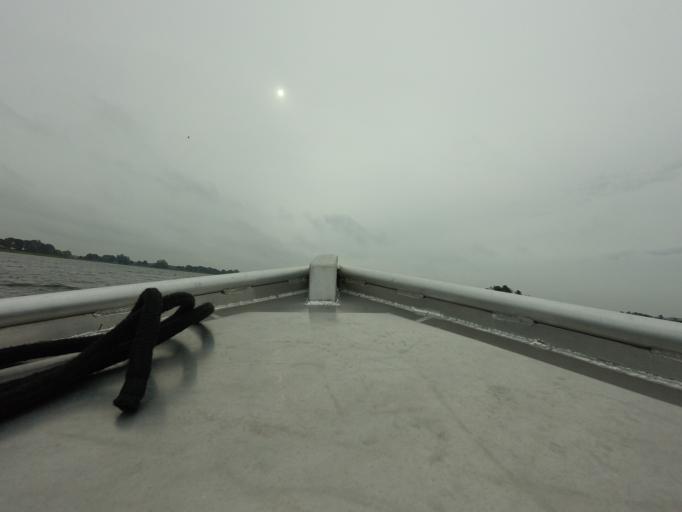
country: NL
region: Overijssel
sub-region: Gemeente Steenwijkerland
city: Blokzijl
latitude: 52.7357
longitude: 5.9974
